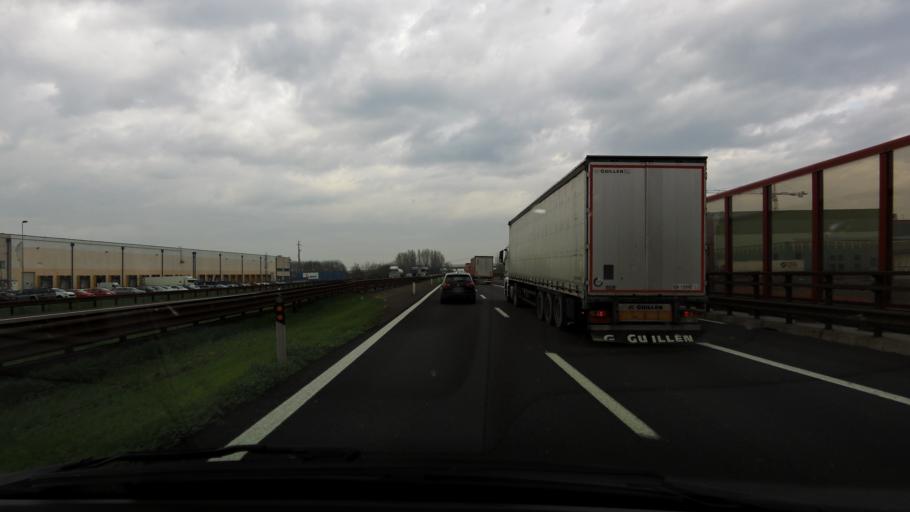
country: IT
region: Emilia-Romagna
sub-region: Provincia di Reggio Emilia
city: Rolo
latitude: 44.8719
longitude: 10.8501
